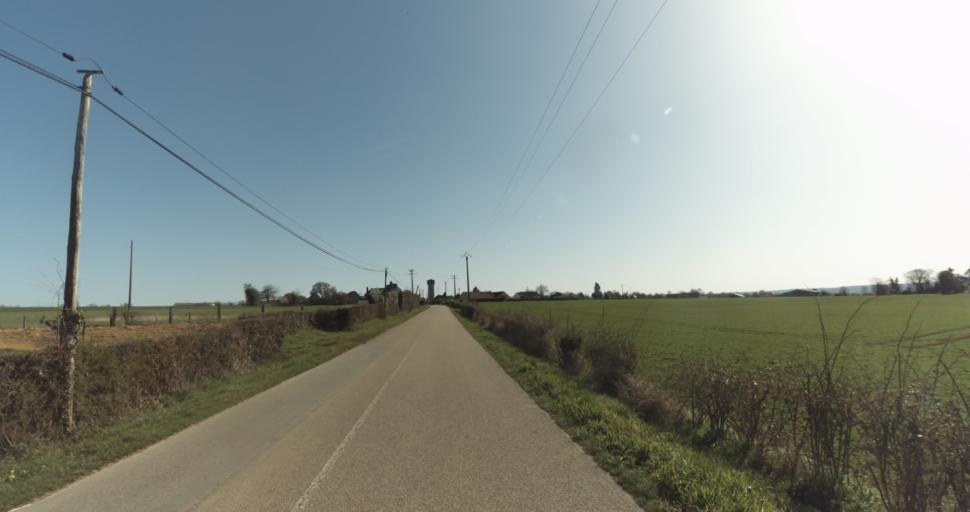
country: FR
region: Lower Normandy
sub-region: Departement de l'Orne
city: Trun
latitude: 48.8744
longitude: 0.0294
